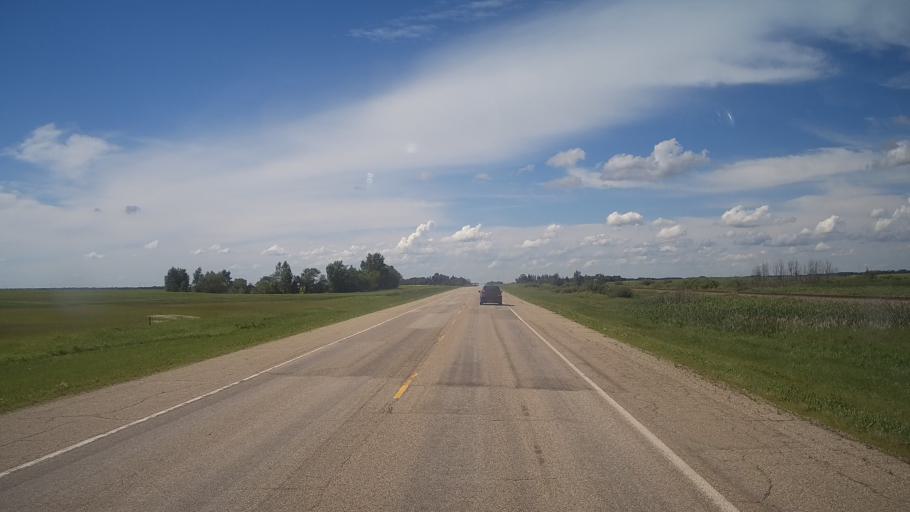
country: CA
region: Saskatchewan
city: Yorkton
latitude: 51.0842
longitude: -102.2511
